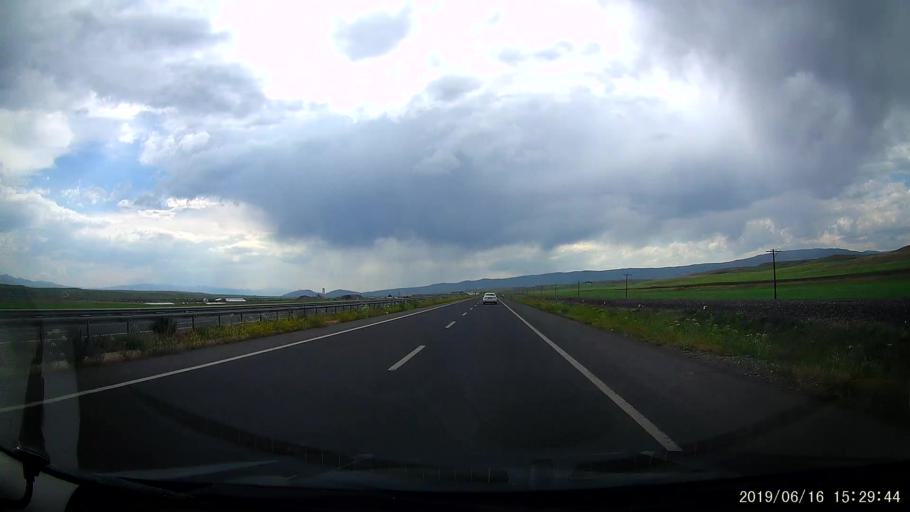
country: TR
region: Erzurum
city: Horasan
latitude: 40.0324
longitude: 42.1245
